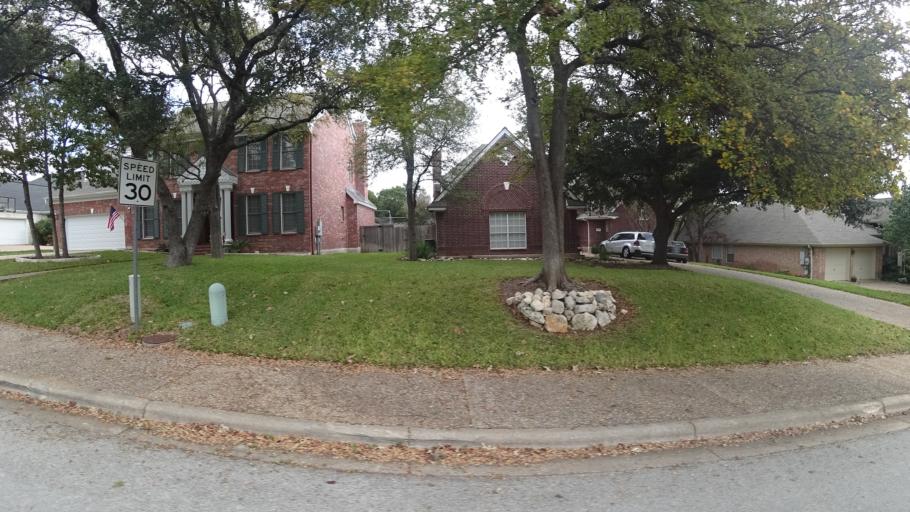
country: US
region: Texas
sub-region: Travis County
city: Barton Creek
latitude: 30.2931
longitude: -97.8843
